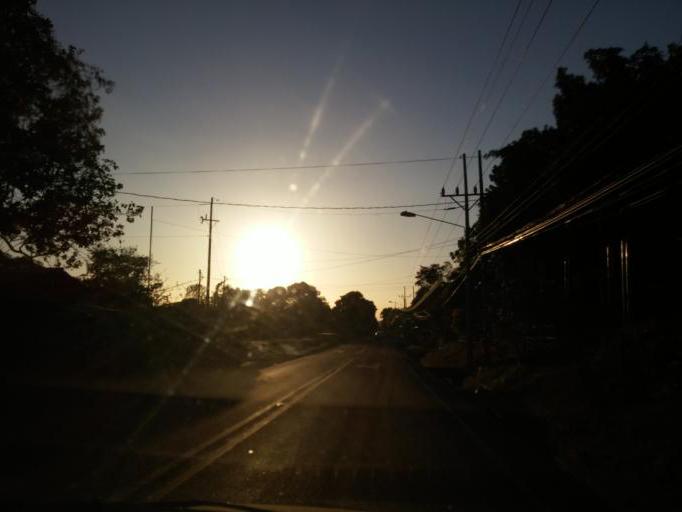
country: CR
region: Alajuela
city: Orotina
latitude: 9.9149
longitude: -84.5351
